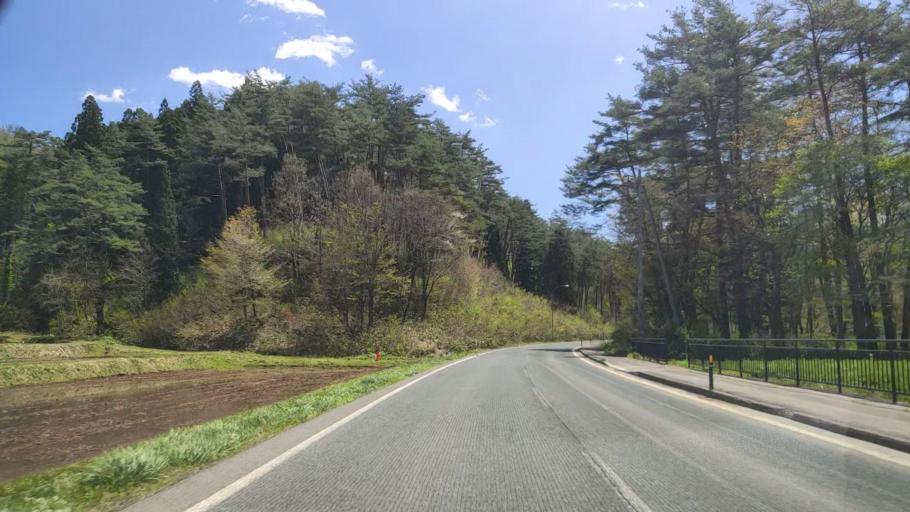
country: JP
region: Yamagata
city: Shinjo
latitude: 38.9056
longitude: 140.3264
